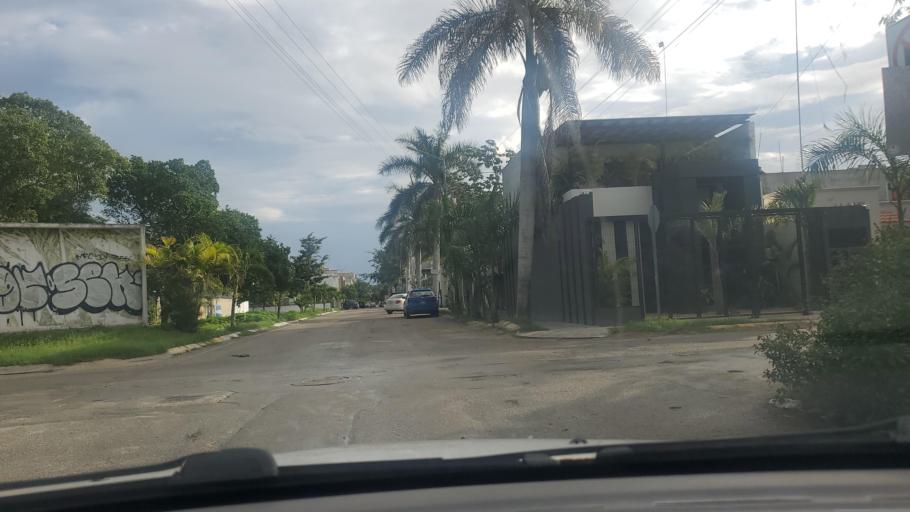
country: MX
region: Quintana Roo
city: Tulum
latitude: 20.2149
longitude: -87.4579
